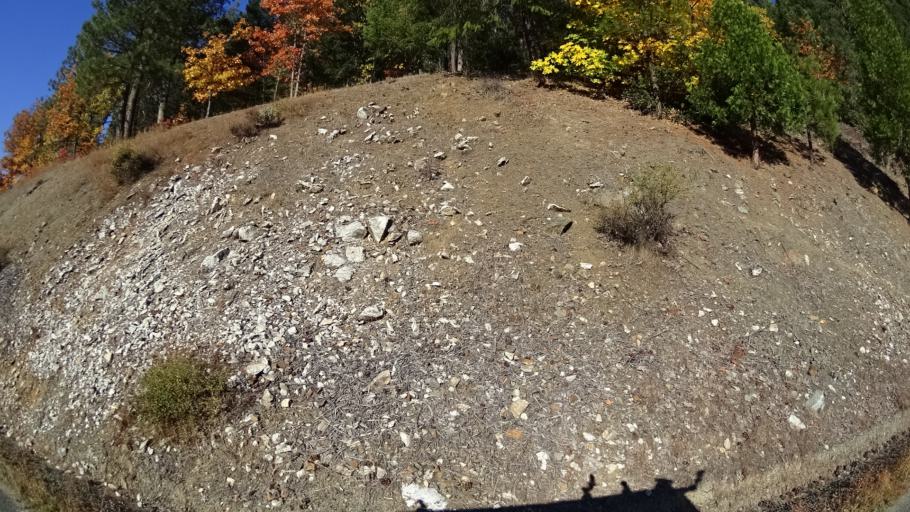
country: US
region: California
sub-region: Siskiyou County
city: Happy Camp
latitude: 41.6448
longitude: -123.0438
